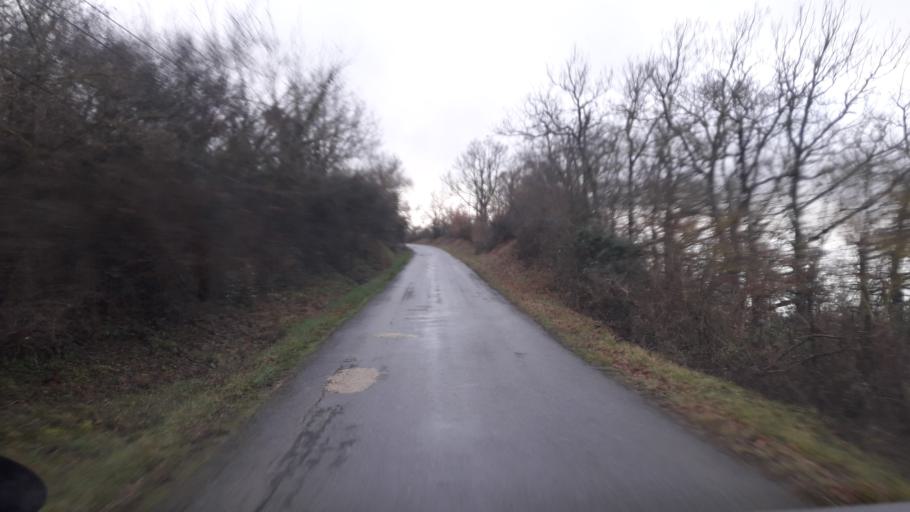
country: FR
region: Midi-Pyrenees
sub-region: Departement de la Haute-Garonne
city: Marquefave
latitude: 43.3111
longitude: 1.2432
